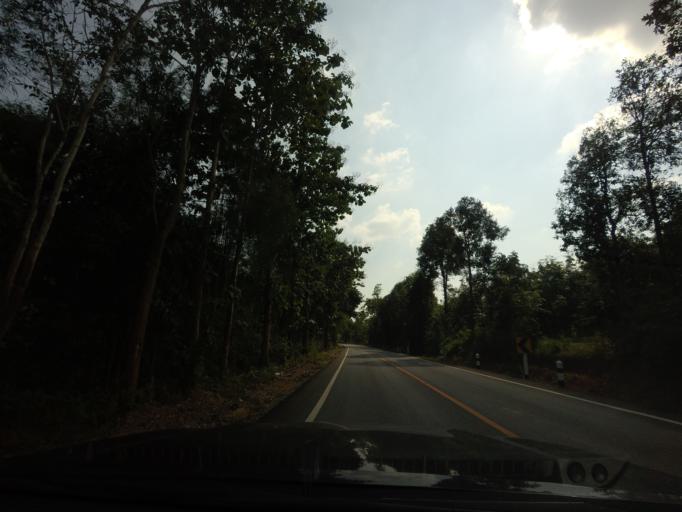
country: TH
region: Nan
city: Santi Suk
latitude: 18.9750
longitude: 100.9288
